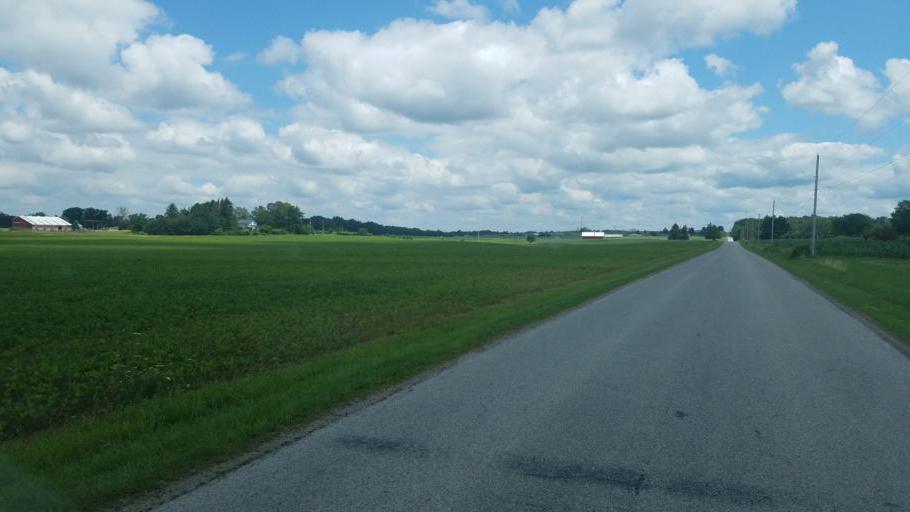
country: US
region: Ohio
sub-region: Richland County
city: Lexington
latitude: 40.6810
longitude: -82.6577
